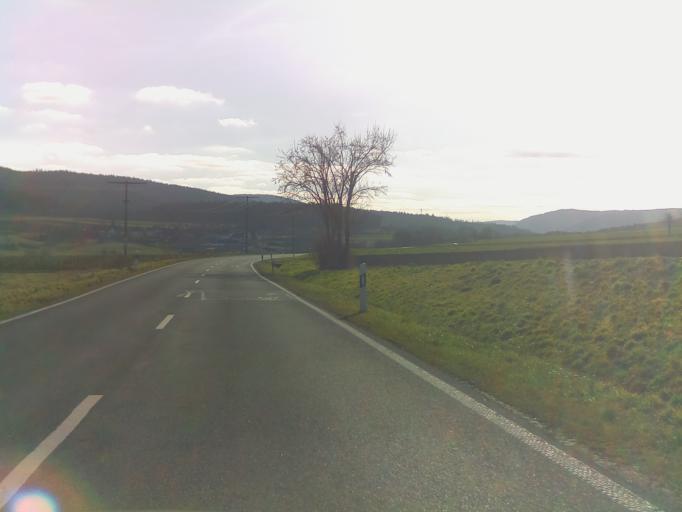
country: DE
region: Bavaria
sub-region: Regierungsbezirk Unterfranken
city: Rollbach
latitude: 49.7558
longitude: 9.2439
